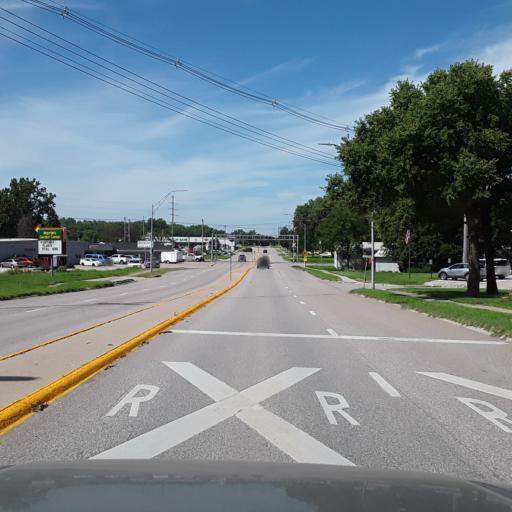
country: US
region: Nebraska
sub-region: Seward County
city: Seward
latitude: 40.9063
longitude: -97.1053
